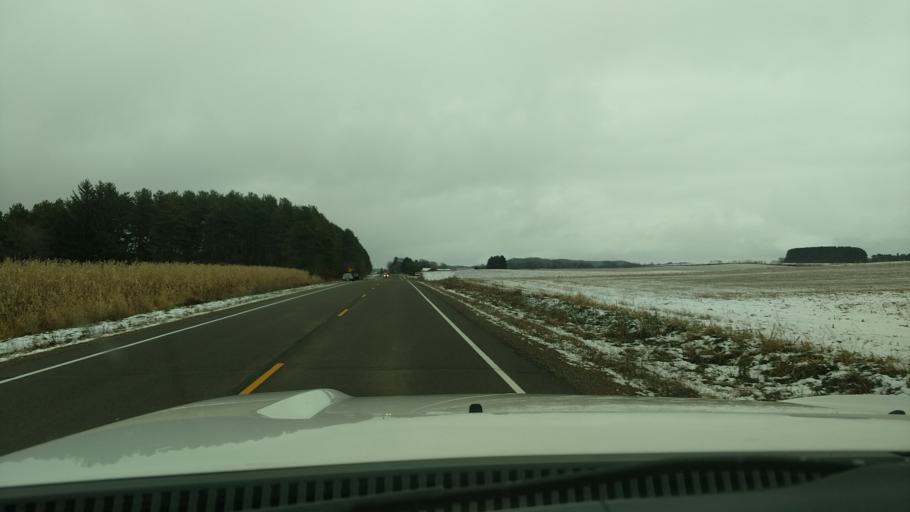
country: US
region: Wisconsin
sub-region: Dunn County
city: Colfax
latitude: 45.1426
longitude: -91.6731
